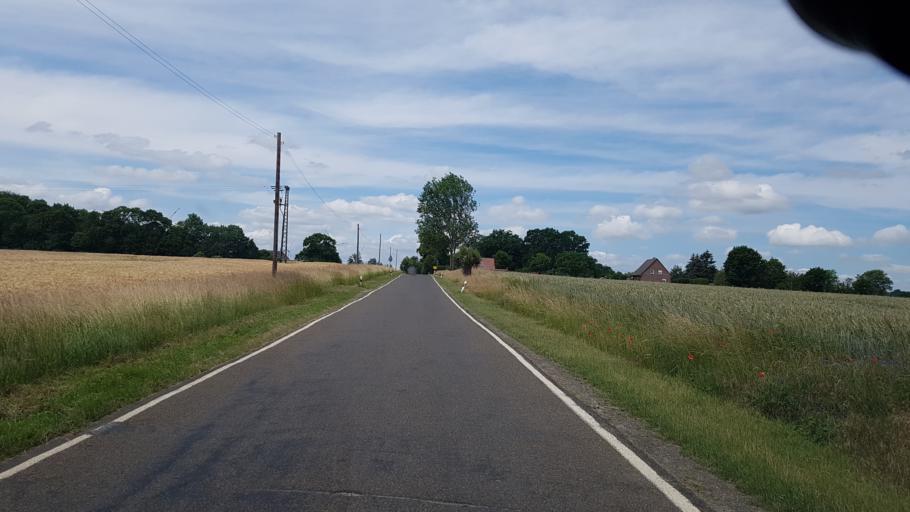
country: DE
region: Mecklenburg-Vorpommern
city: Strasburg
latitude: 53.4433
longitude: 13.7752
